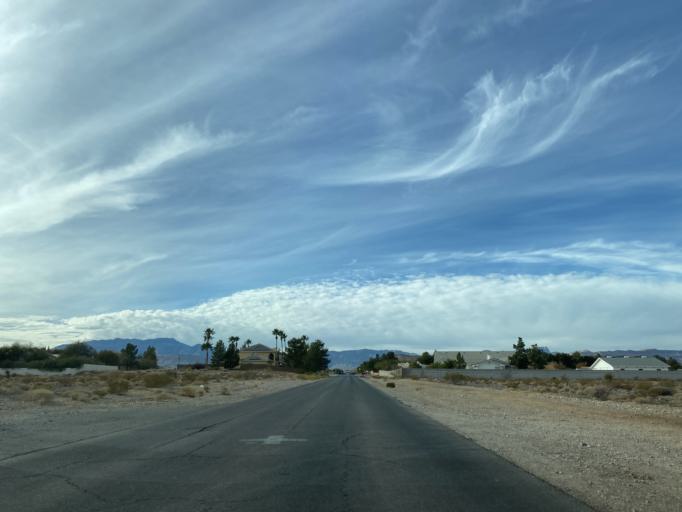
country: US
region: Nevada
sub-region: Clark County
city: Enterprise
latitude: 36.0336
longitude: -115.2720
